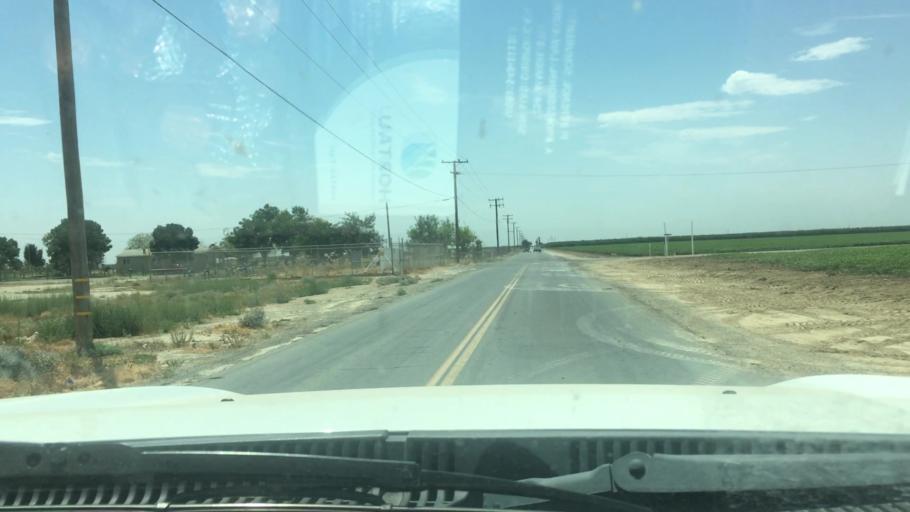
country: US
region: California
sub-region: Tulare County
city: Tipton
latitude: 36.0658
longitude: -119.3208
